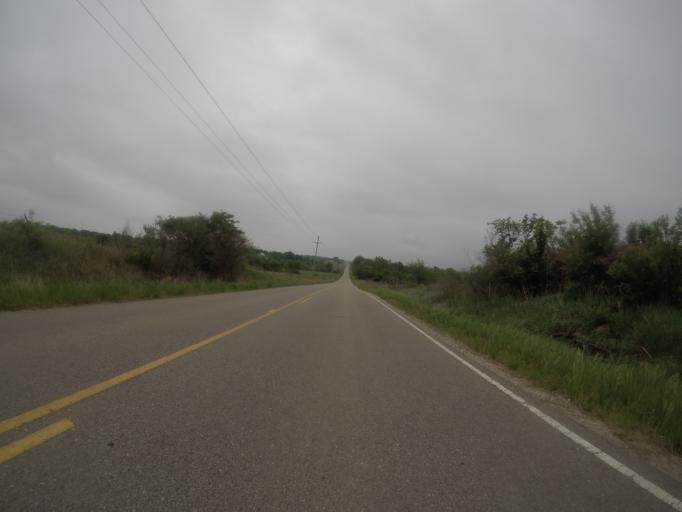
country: US
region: Kansas
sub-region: Pottawatomie County
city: Westmoreland
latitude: 39.5222
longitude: -96.2689
